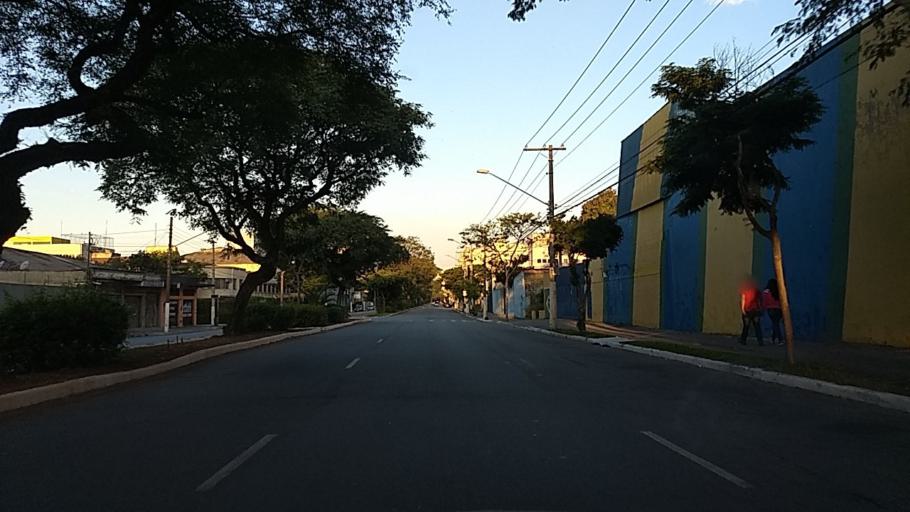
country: BR
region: Sao Paulo
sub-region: Sao Paulo
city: Sao Paulo
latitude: -23.5244
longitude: -46.6164
